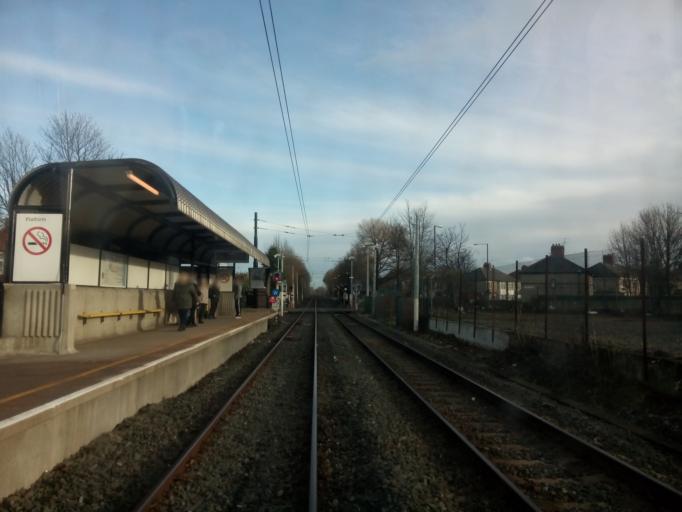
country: GB
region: England
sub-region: Newcastle upon Tyne
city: Hazlerigg
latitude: 55.0134
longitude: -1.6451
